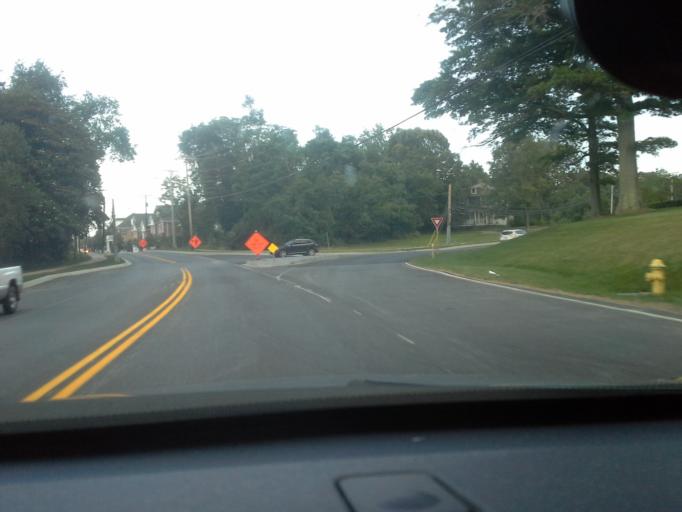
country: US
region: Maryland
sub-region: Calvert County
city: Prince Frederick
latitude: 38.5411
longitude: -76.5858
